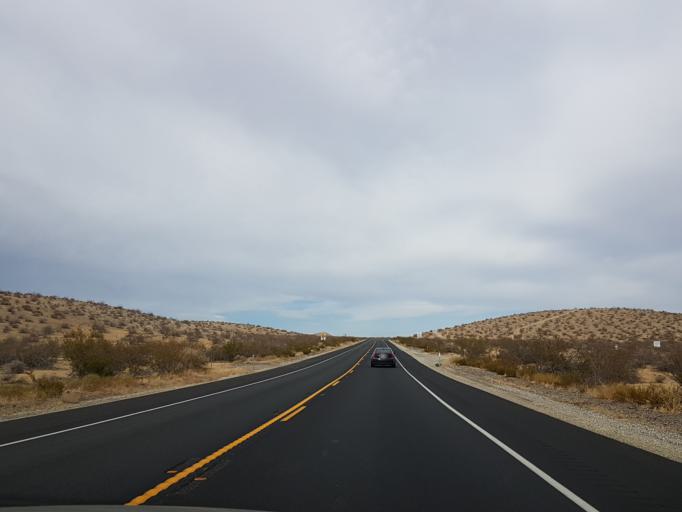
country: US
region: California
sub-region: Kern County
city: Ridgecrest
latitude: 35.4557
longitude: -117.6545
